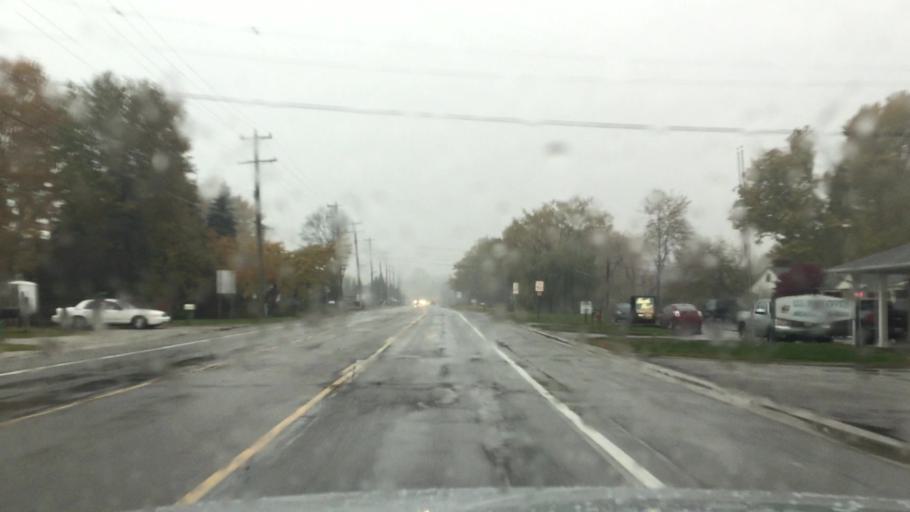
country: US
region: Michigan
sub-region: Macomb County
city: New Baltimore
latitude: 42.6912
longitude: -82.6892
